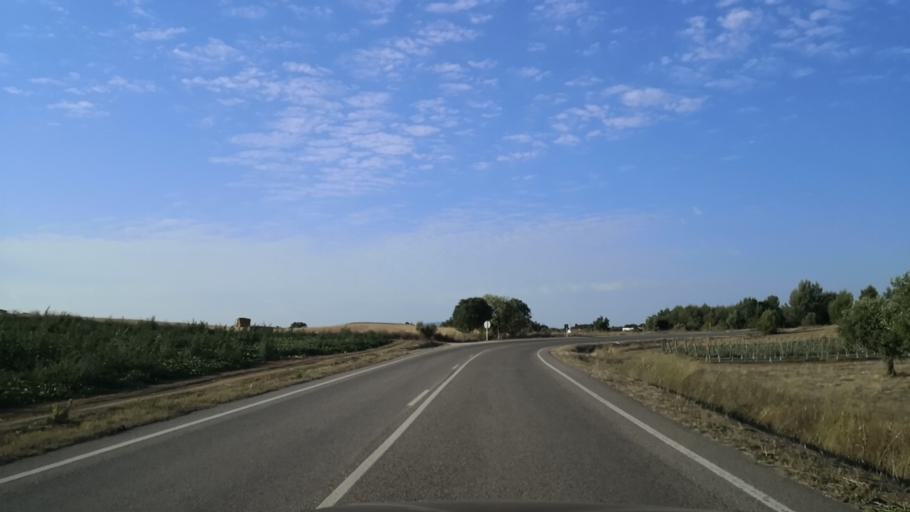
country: PT
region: Santarem
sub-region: Santarem
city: Santarem
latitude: 39.3283
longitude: -8.6624
